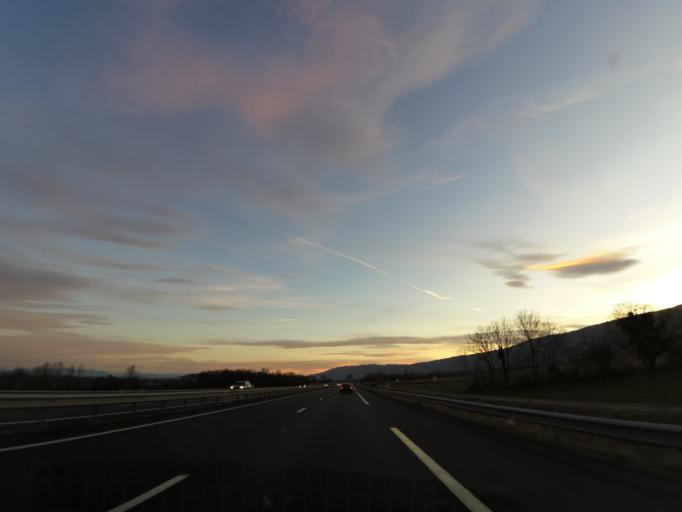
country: FR
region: Rhone-Alpes
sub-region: Departement de l'Ain
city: Chatillon-en-Michaille
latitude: 46.1249
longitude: 5.7981
